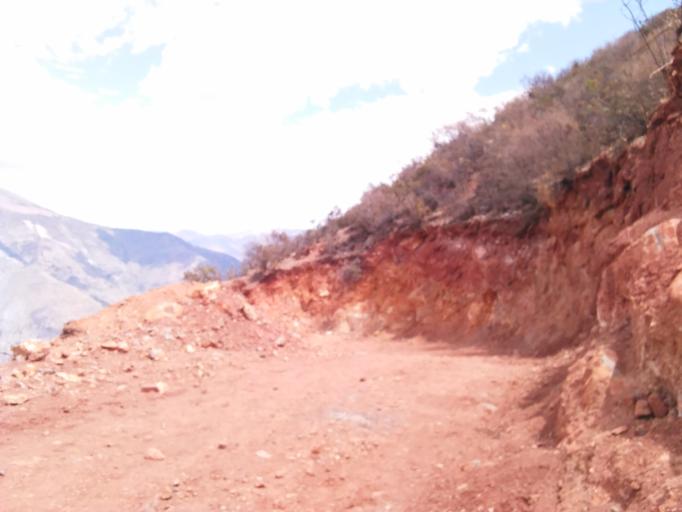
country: PE
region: Ayacucho
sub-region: Provincia de Victor Fajardo
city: Canaria
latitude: -13.8816
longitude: -73.9352
